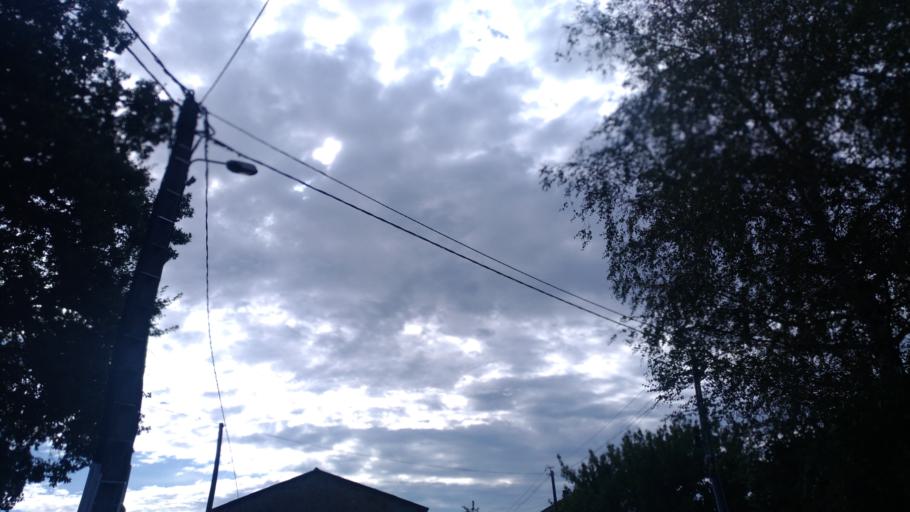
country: FR
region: Midi-Pyrenees
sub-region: Departement du Tarn
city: Puygouzon
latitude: 43.9156
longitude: 2.1798
